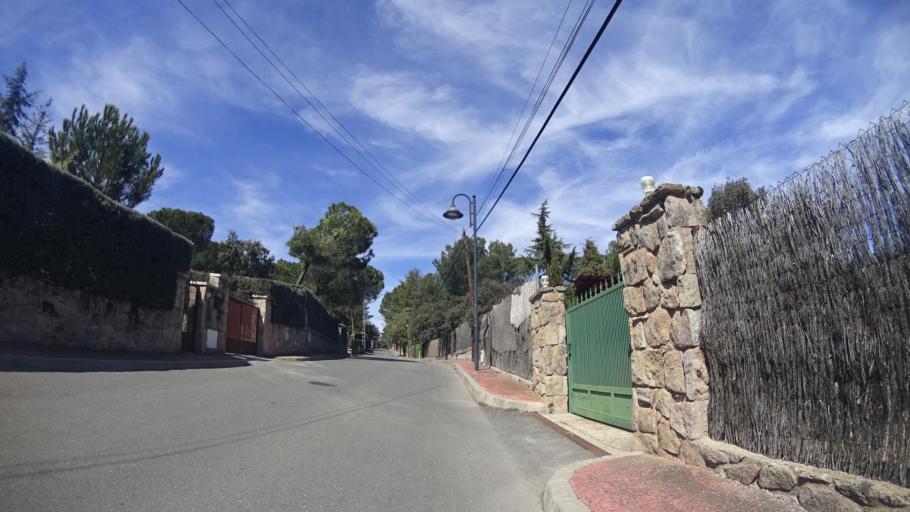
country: ES
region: Madrid
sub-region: Provincia de Madrid
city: Galapagar
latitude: 40.5917
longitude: -3.9827
